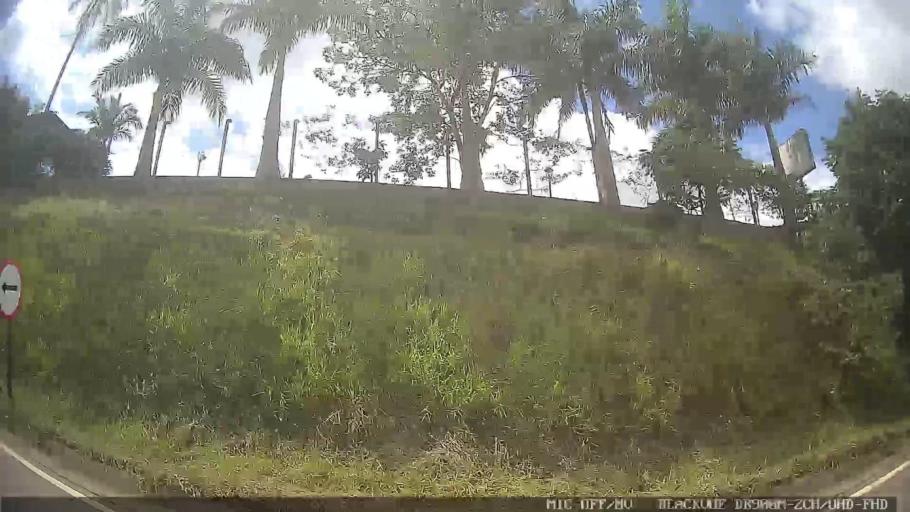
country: BR
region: Minas Gerais
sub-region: Extrema
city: Extrema
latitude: -22.8039
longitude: -46.4492
